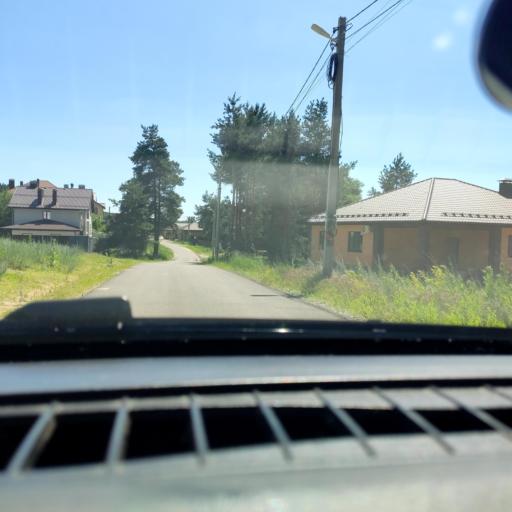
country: RU
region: Voronezj
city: Podgornoye
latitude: 51.7954
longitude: 39.1359
